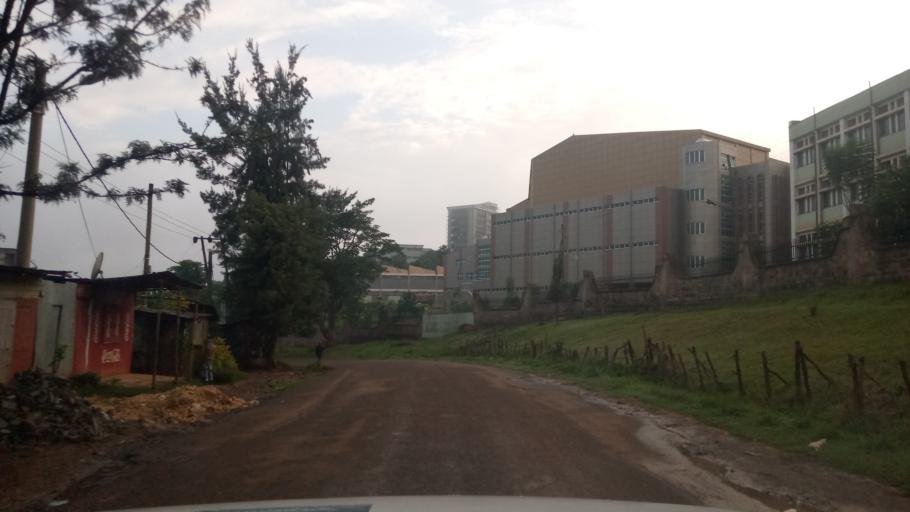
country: ET
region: Oromiya
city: Jima
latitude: 7.6802
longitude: 36.8507
